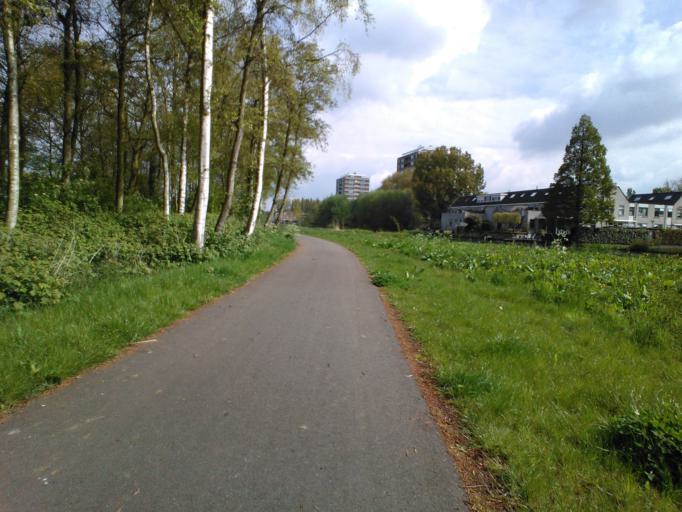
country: NL
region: South Holland
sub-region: Gemeente Vlaardingen
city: Vlaardingen
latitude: 51.9137
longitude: 4.3093
